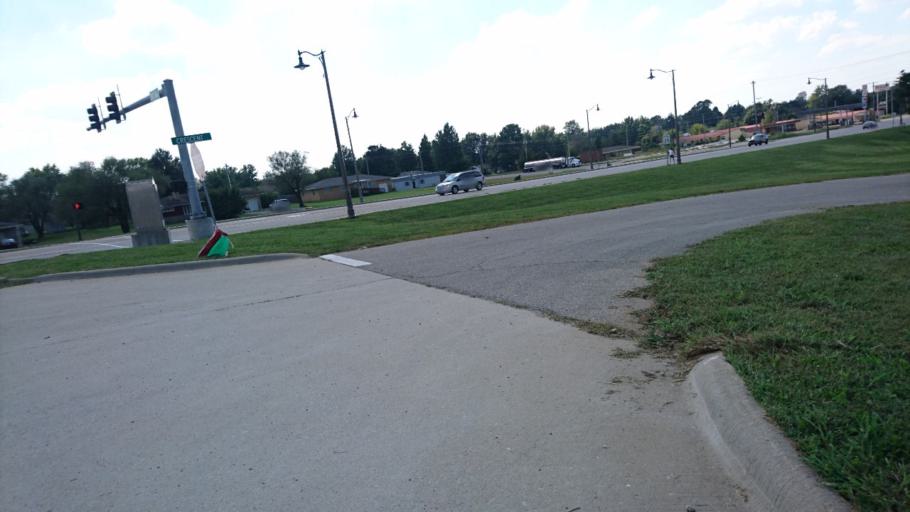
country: US
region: Missouri
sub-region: Laclede County
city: Lebanon
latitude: 37.6841
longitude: -92.6433
